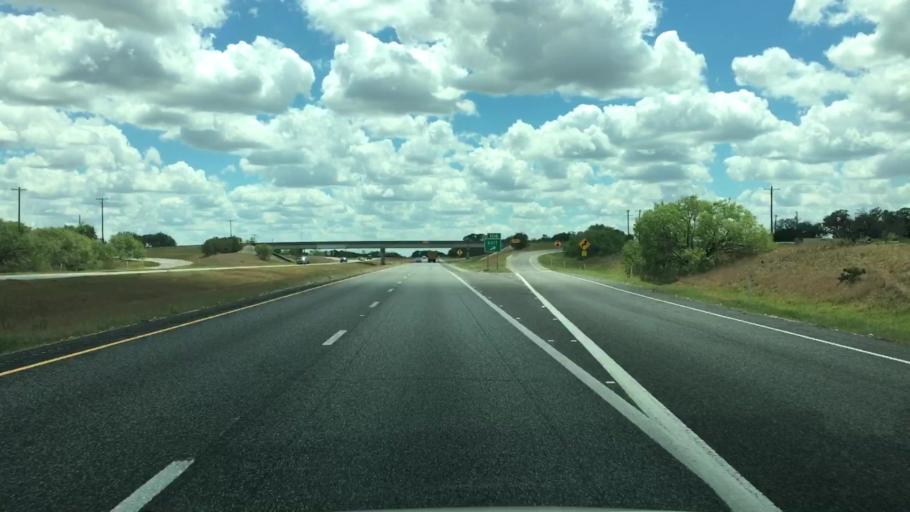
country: US
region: Texas
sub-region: Atascosa County
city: Pleasanton
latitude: 28.9487
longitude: -98.4359
